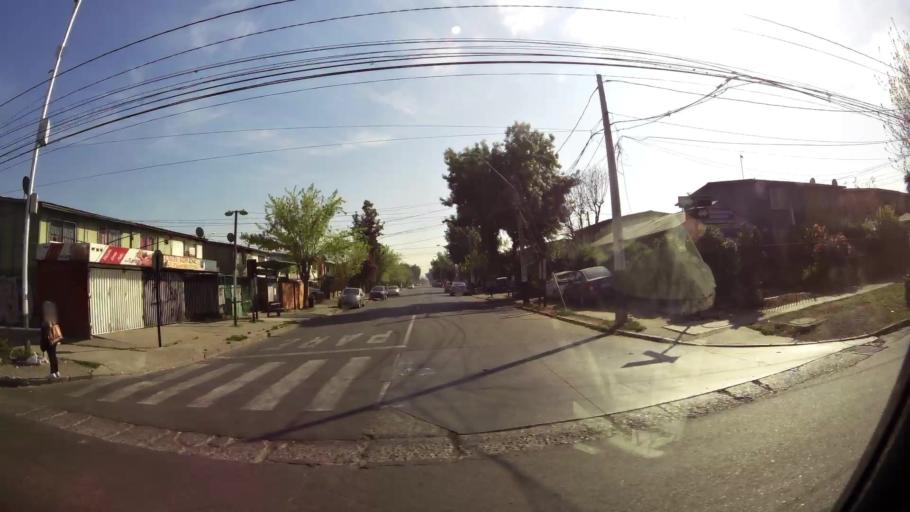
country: CL
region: Santiago Metropolitan
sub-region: Provincia de Santiago
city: Lo Prado
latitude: -33.4664
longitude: -70.7476
